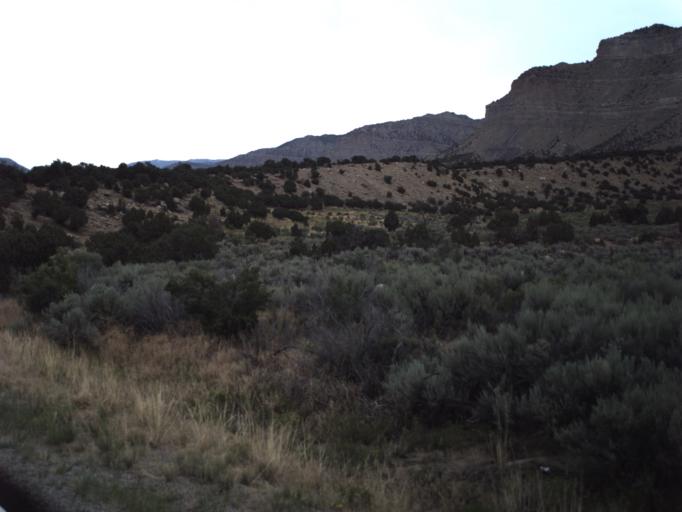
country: US
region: Utah
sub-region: Carbon County
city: East Carbon City
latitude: 39.4699
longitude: -110.3966
